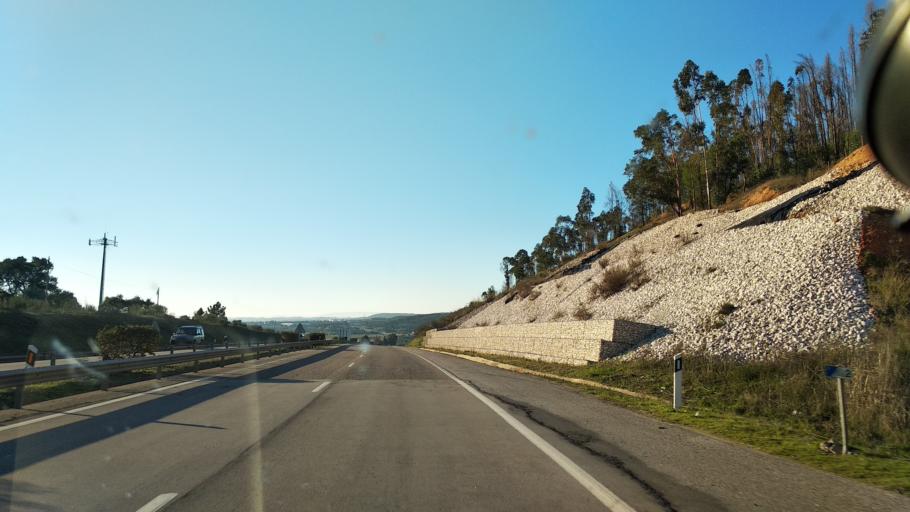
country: PT
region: Santarem
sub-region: Abrantes
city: Tramagal
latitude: 39.4810
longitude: -8.2371
